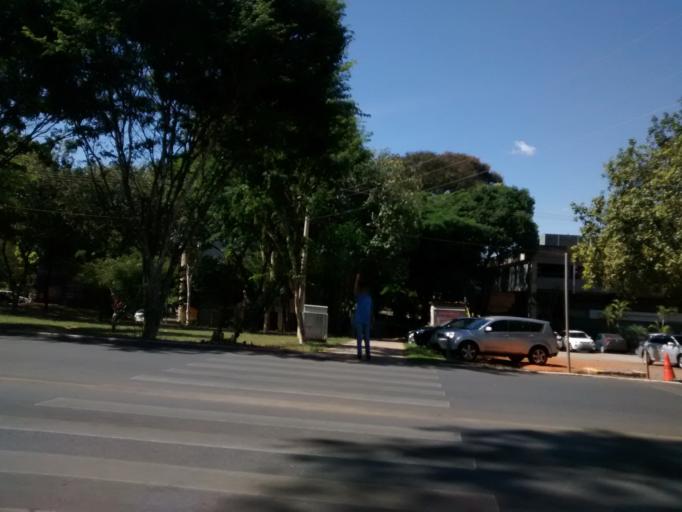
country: BR
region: Federal District
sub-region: Brasilia
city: Brasilia
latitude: -15.7526
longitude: -47.8910
